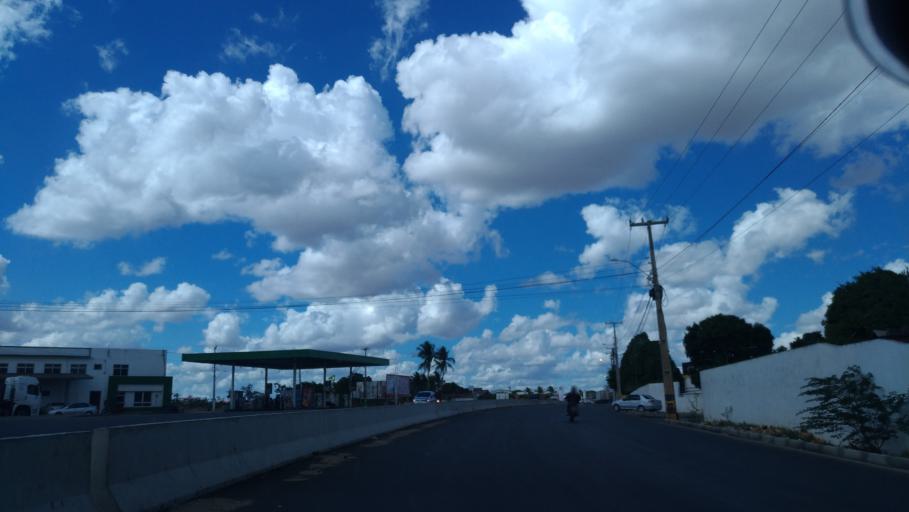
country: BR
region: Alagoas
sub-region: Arapiraca
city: Arapiraca
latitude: -9.7529
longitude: -36.6383
